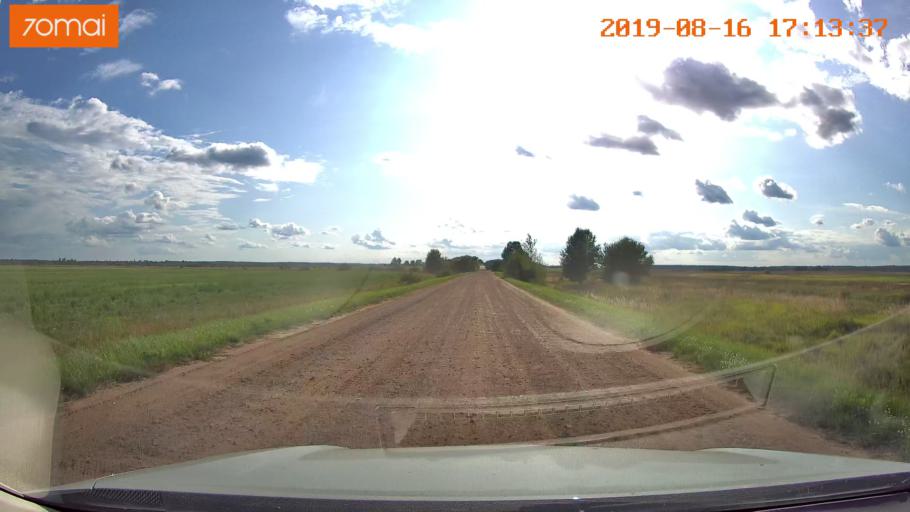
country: BY
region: Mogilev
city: Hlusha
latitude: 53.1887
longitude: 28.8731
